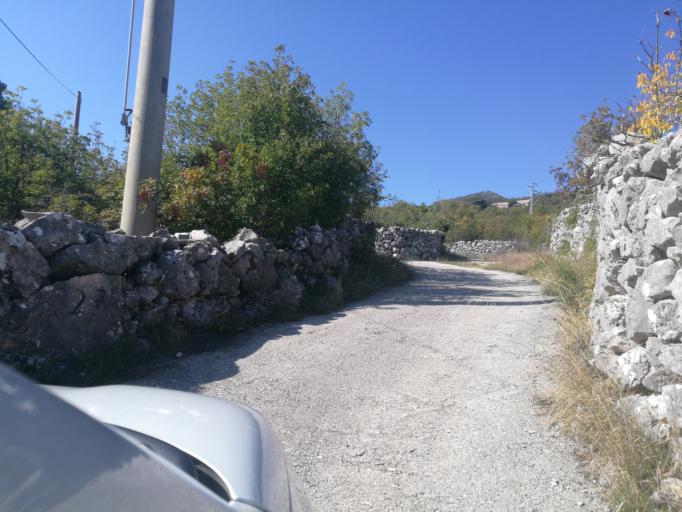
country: HR
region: Splitsko-Dalmatinska
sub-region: Grad Omis
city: Omis
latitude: 43.5173
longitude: 16.7325
